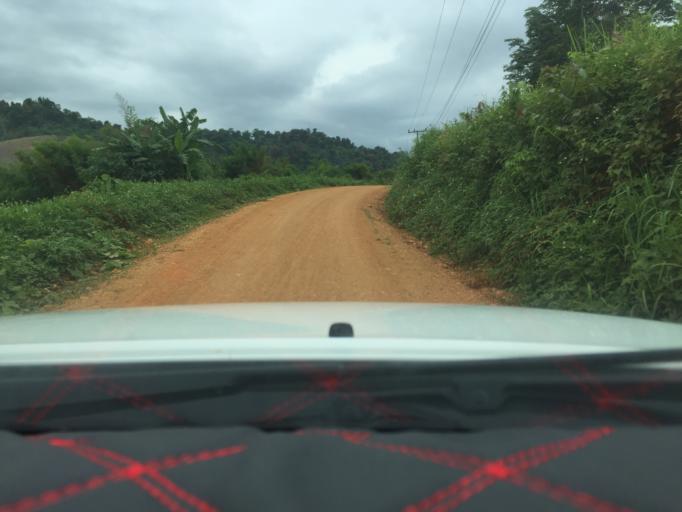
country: TH
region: Phayao
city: Phu Sang
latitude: 19.7689
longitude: 100.5499
